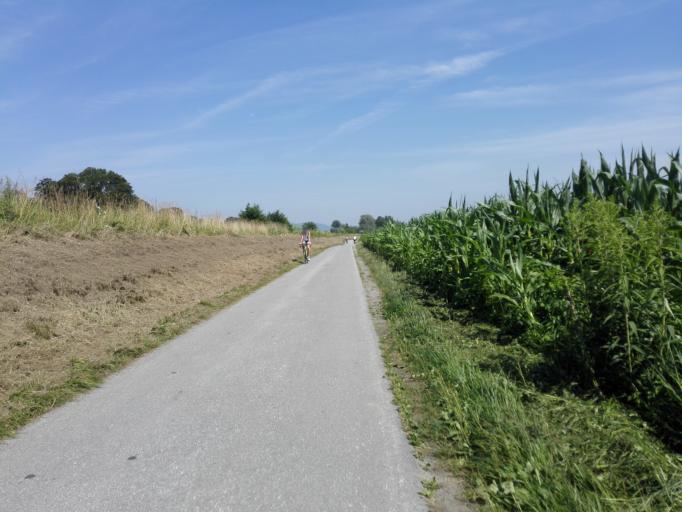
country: AT
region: Styria
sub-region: Politischer Bezirk Graz-Umgebung
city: Gossendorf
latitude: 46.9765
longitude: 15.4733
